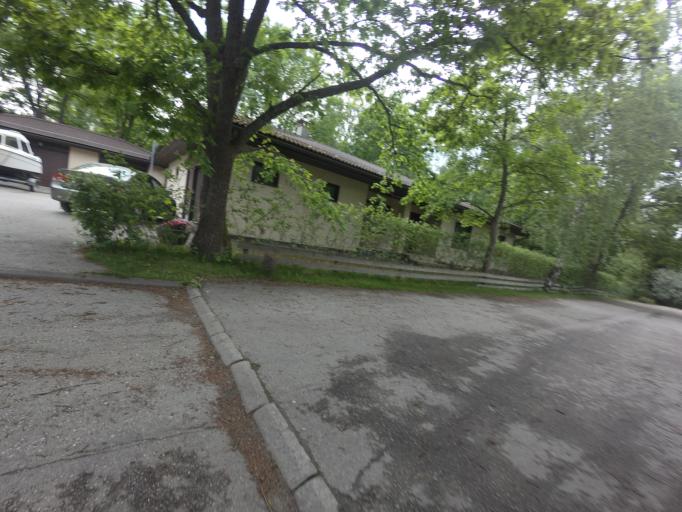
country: FI
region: Uusimaa
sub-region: Helsinki
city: Koukkuniemi
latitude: 60.1605
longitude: 24.7322
